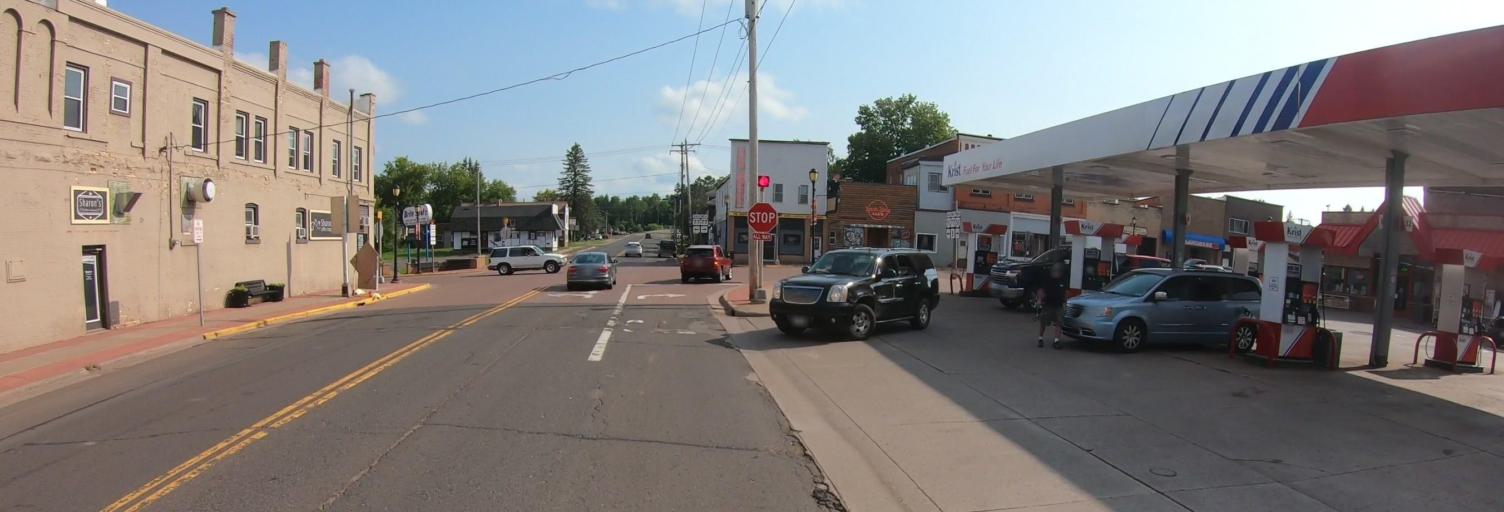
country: US
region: Wisconsin
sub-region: Iron County
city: Hurley
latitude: 46.4503
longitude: -90.1819
